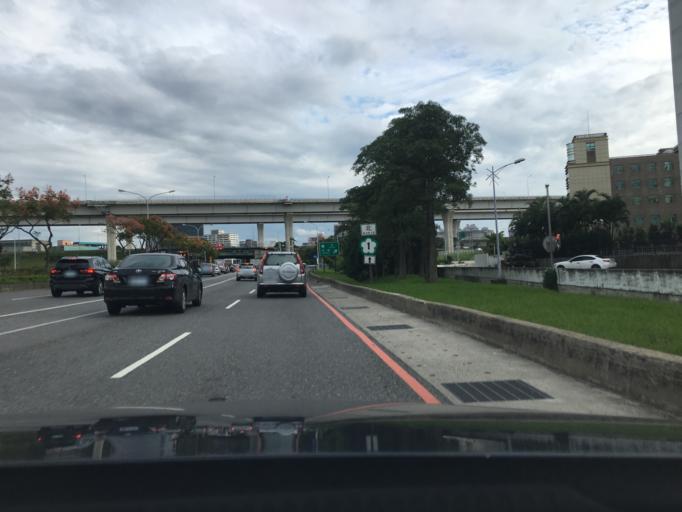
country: TW
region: Taiwan
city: Taoyuan City
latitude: 25.0399
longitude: 121.2961
